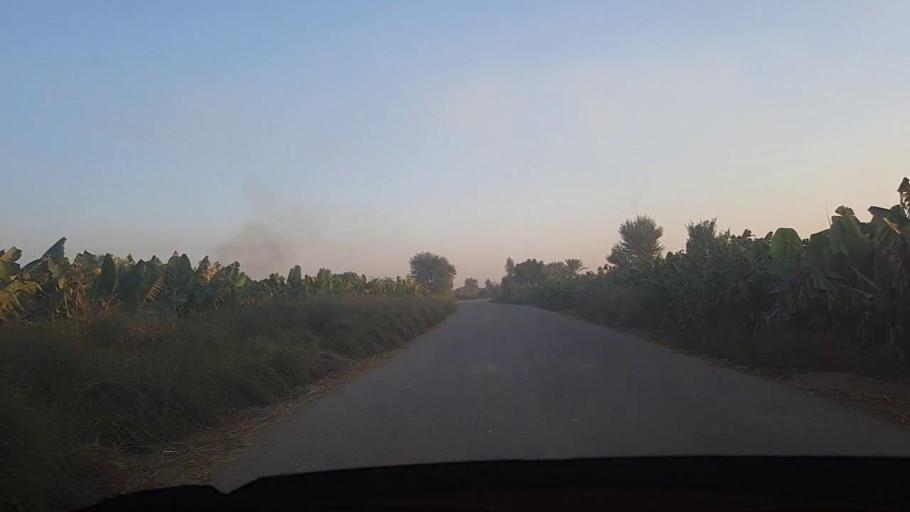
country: PK
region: Sindh
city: Sobhadero
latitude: 27.3451
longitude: 68.3769
